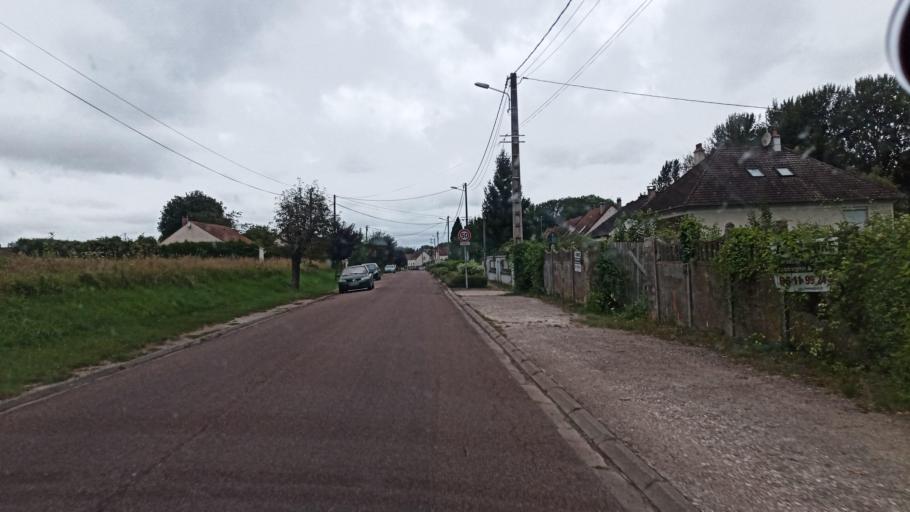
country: FR
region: Ile-de-France
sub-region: Departement de Seine-et-Marne
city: Voulx
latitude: 48.2793
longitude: 2.9761
